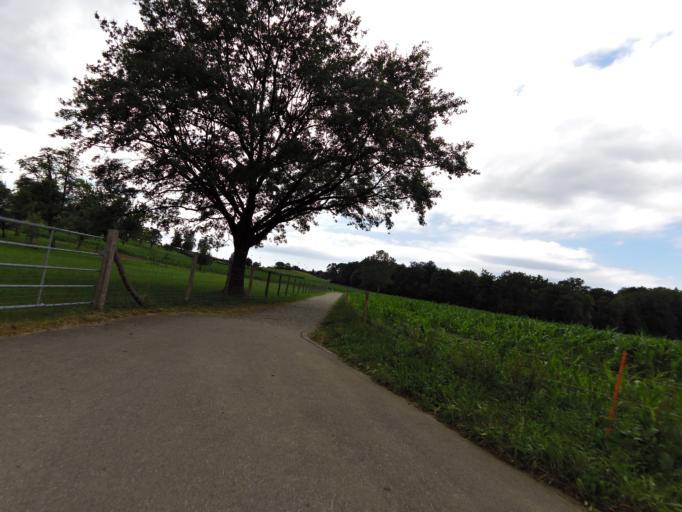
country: CH
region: Zurich
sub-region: Bezirk Zuerich
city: Zuerich (Kreis 10)
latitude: 47.4071
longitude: 8.5032
